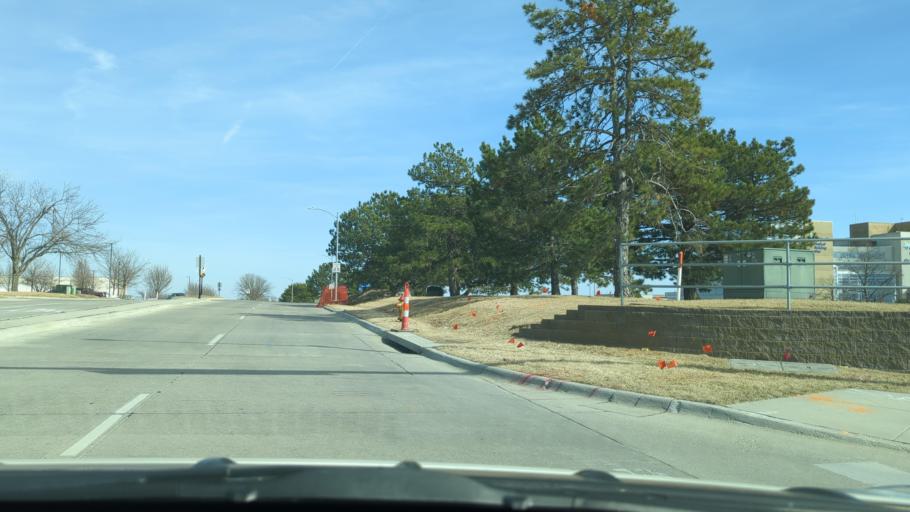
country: US
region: Nebraska
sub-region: Sarpy County
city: Papillion
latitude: 41.1375
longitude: -96.0427
